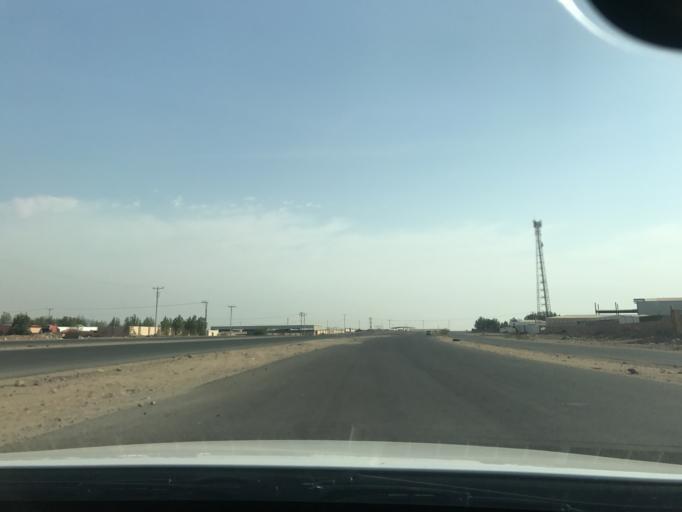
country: SA
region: Makkah
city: Al Jumum
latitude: 21.4458
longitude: 39.5190
